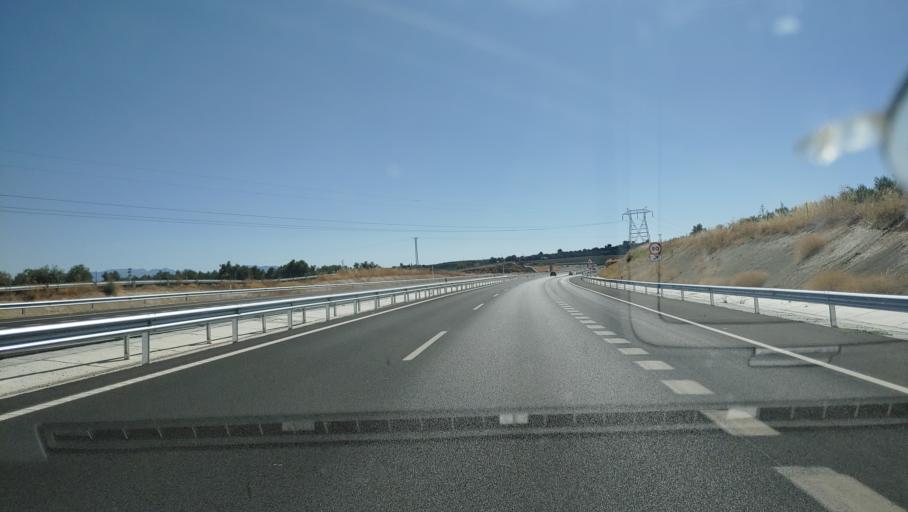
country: ES
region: Andalusia
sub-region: Provincia de Jaen
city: Sabiote
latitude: 38.0349
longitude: -3.3275
